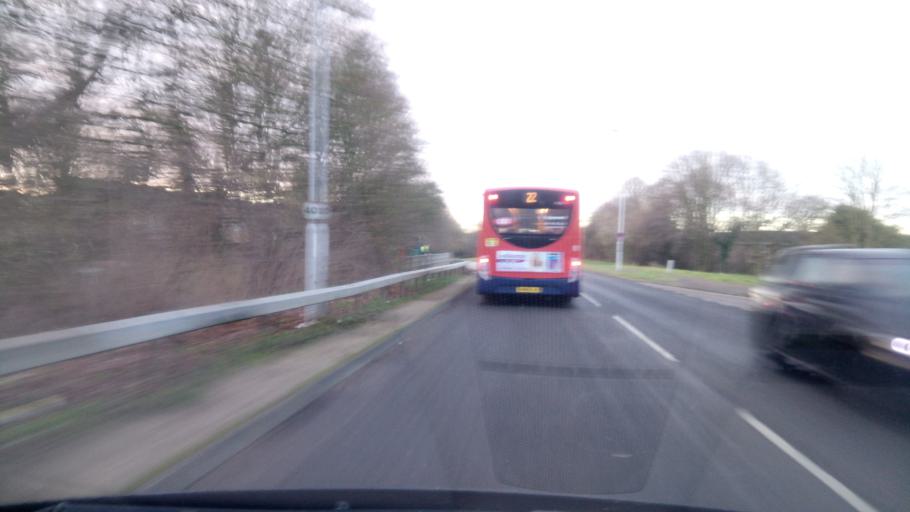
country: GB
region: England
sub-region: Peterborough
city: Marholm
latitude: 52.5817
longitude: -0.2883
